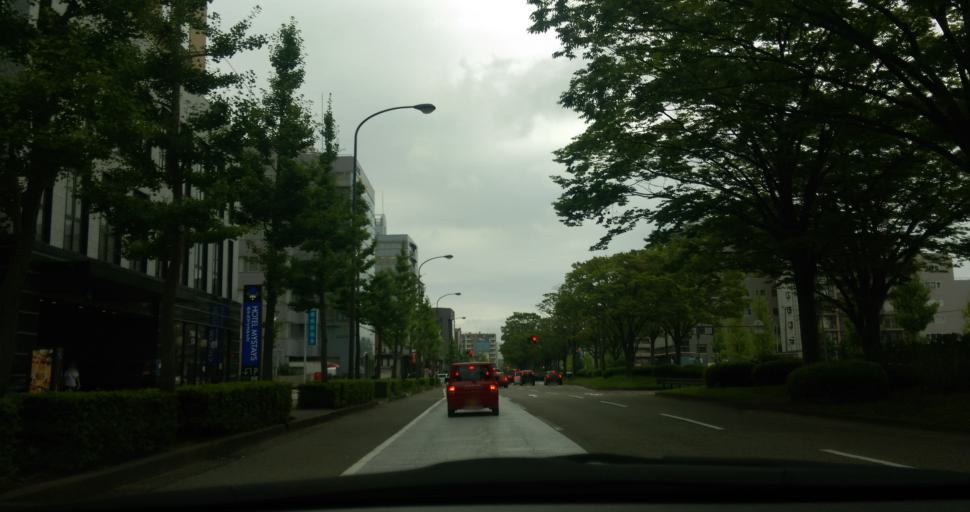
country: JP
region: Ishikawa
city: Kanazawa-shi
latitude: 36.5801
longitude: 136.6443
